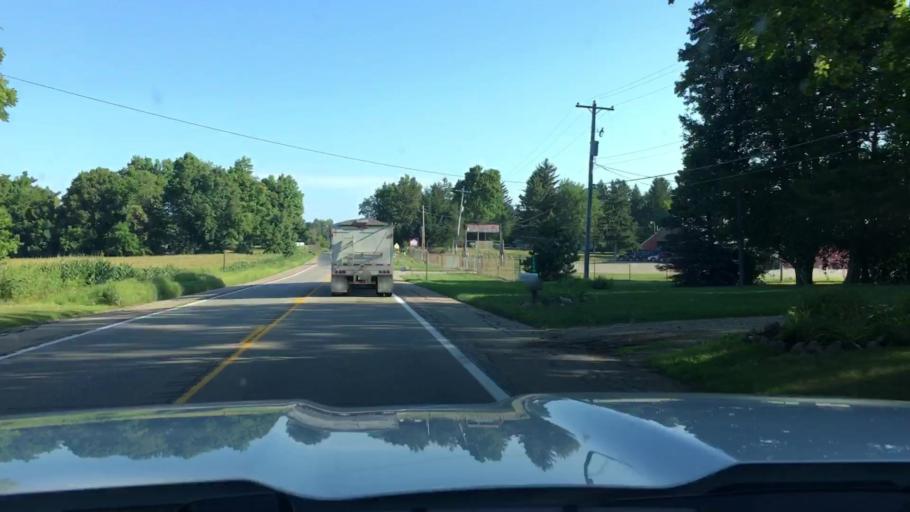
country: US
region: Michigan
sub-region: Ionia County
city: Ionia
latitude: 43.0147
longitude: -85.0751
